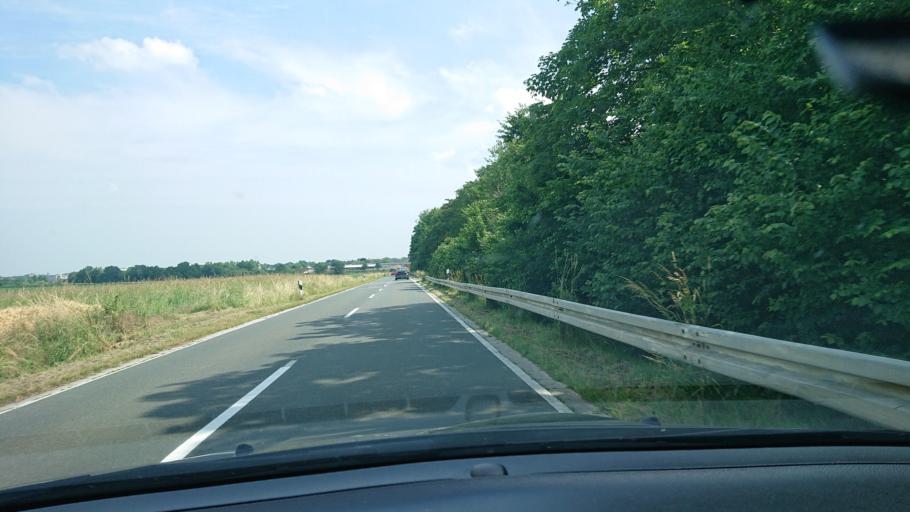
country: DE
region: North Rhine-Westphalia
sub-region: Regierungsbezirk Arnsberg
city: Soest
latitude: 51.5510
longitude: 8.0774
